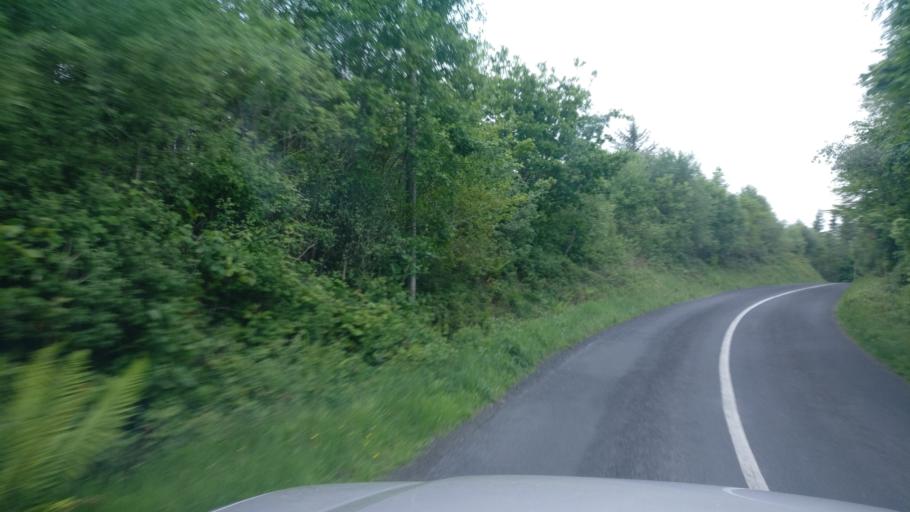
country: IE
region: Connaught
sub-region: County Galway
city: Gort
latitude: 53.0584
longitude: -8.6637
